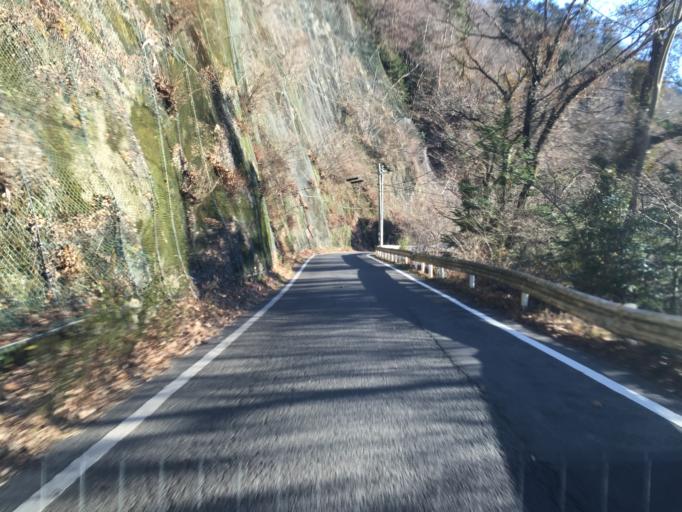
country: JP
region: Fukushima
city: Iwaki
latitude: 37.1662
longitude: 140.8281
